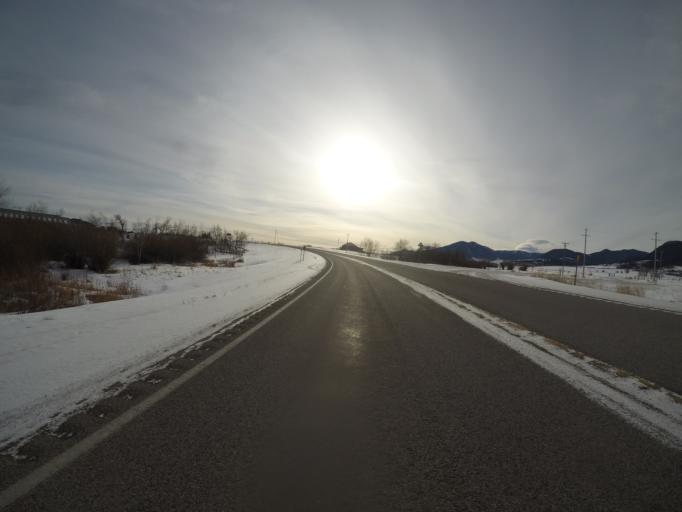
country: US
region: Montana
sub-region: Carbon County
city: Red Lodge
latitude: 45.2160
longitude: -109.2801
